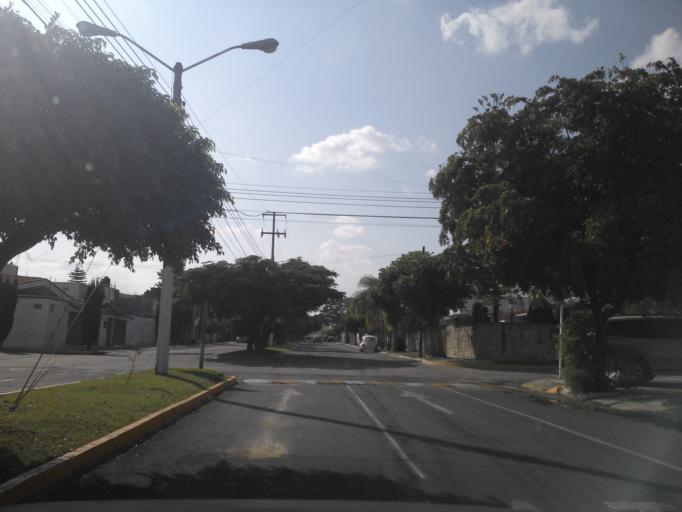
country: MX
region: Jalisco
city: Guadalajara
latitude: 20.6572
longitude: -103.4100
